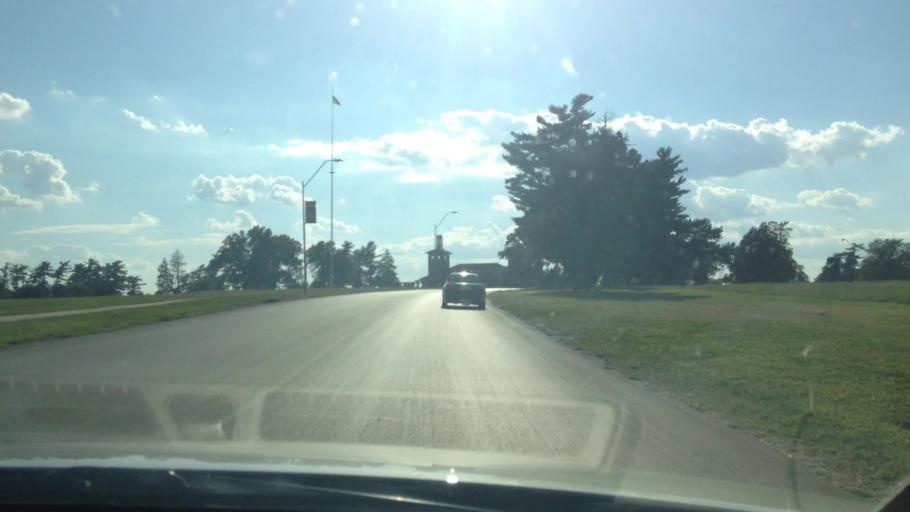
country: US
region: Missouri
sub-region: Jackson County
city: Raytown
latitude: 39.0078
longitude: -94.5368
